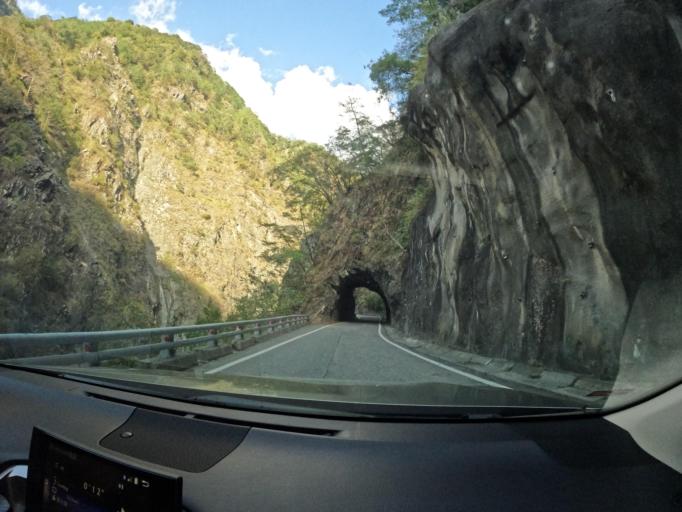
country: TW
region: Taiwan
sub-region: Taitung
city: Taitung
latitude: 23.1740
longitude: 121.0313
